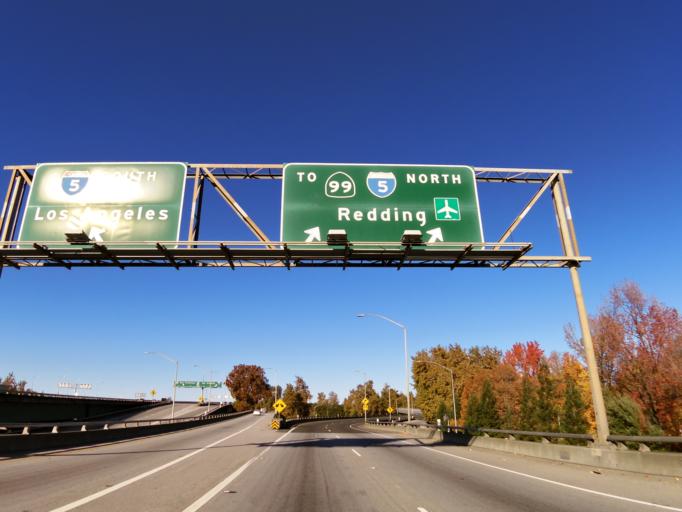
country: US
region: California
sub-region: Sacramento County
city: Sacramento
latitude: 38.5678
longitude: -121.5071
